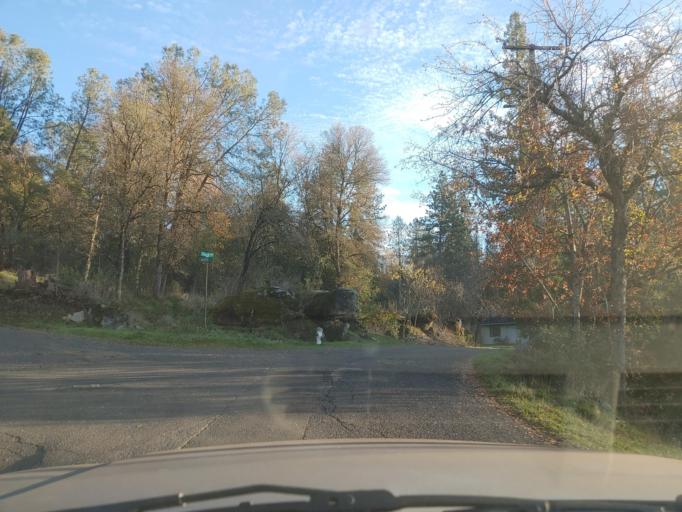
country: US
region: California
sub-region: Tuolumne County
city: Columbia
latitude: 38.0321
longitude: -120.4035
